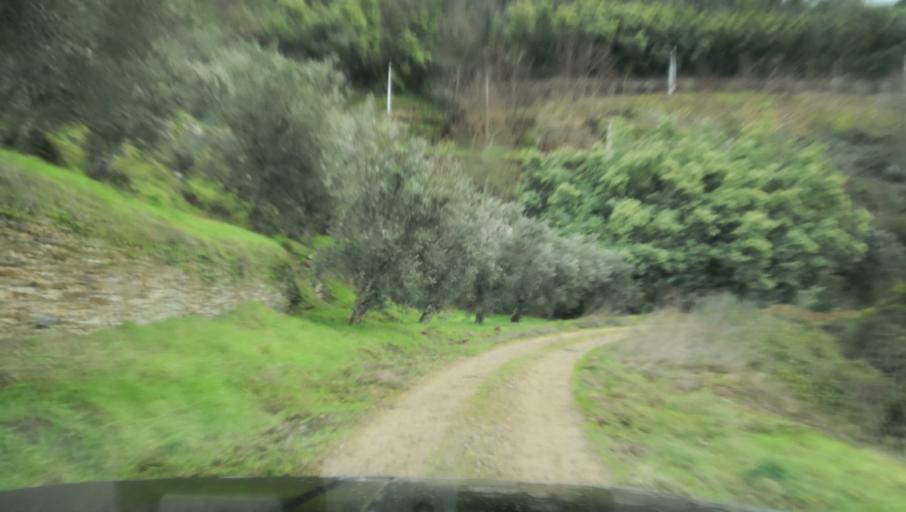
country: PT
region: Vila Real
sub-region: Vila Real
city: Vila Real
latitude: 41.2727
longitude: -7.7376
